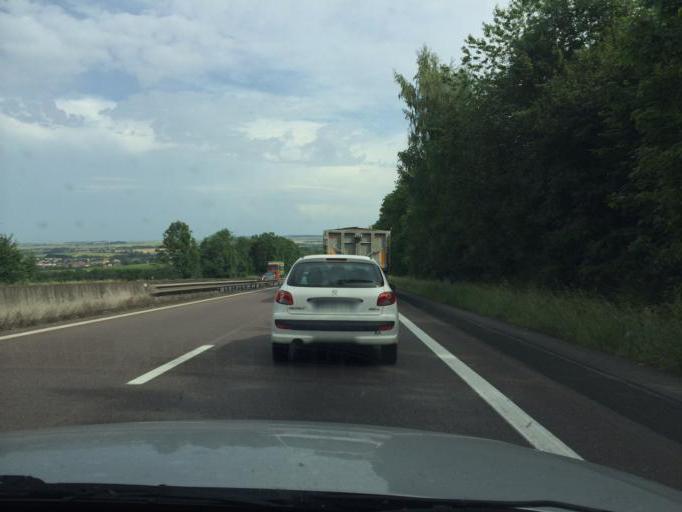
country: FR
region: Lorraine
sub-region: Departement de Meurthe-et-Moselle
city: Ludres
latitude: 48.6341
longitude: 6.1743
